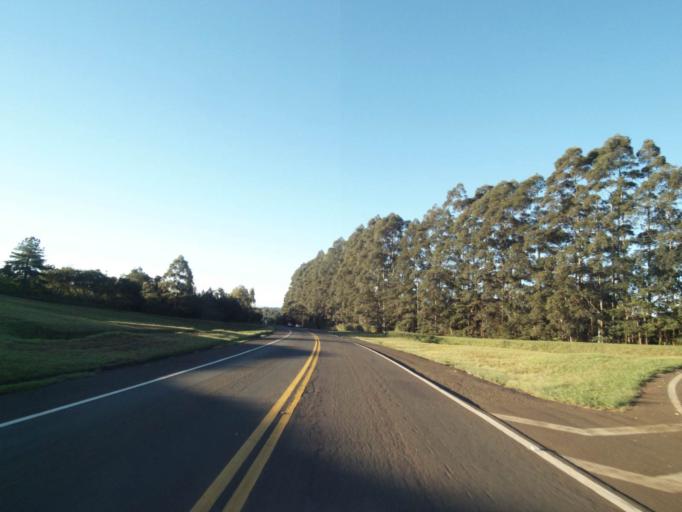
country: BR
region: Parana
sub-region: Faxinal
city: Faxinal
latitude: -23.9069
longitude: -51.1920
